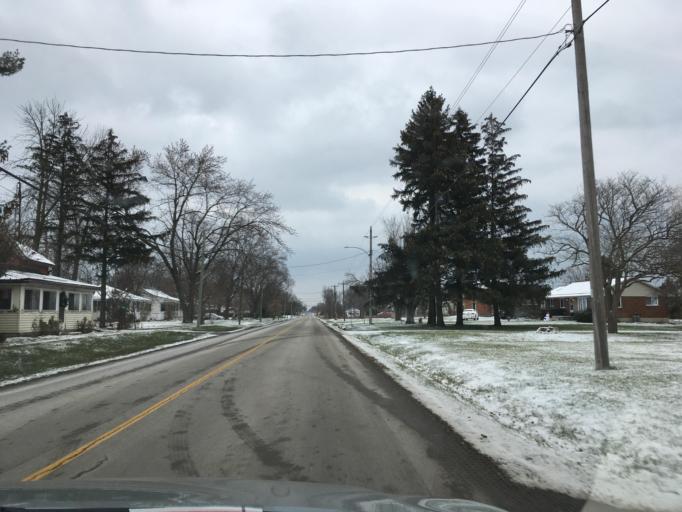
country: CA
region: Ontario
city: Norfolk County
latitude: 42.8110
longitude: -80.0703
